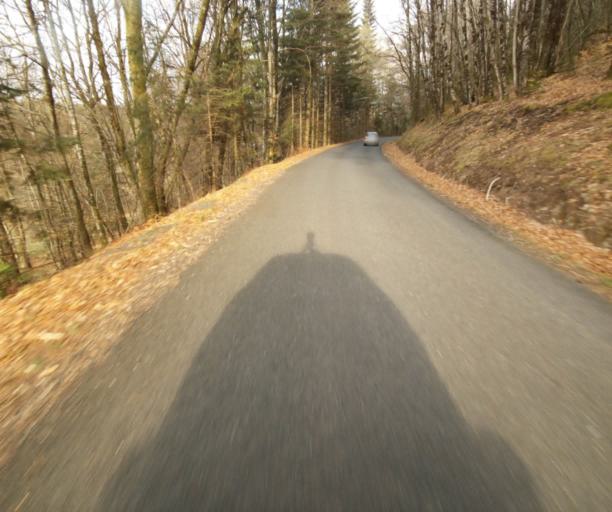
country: FR
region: Limousin
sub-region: Departement de la Correze
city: Correze
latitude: 45.4158
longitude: 1.9043
